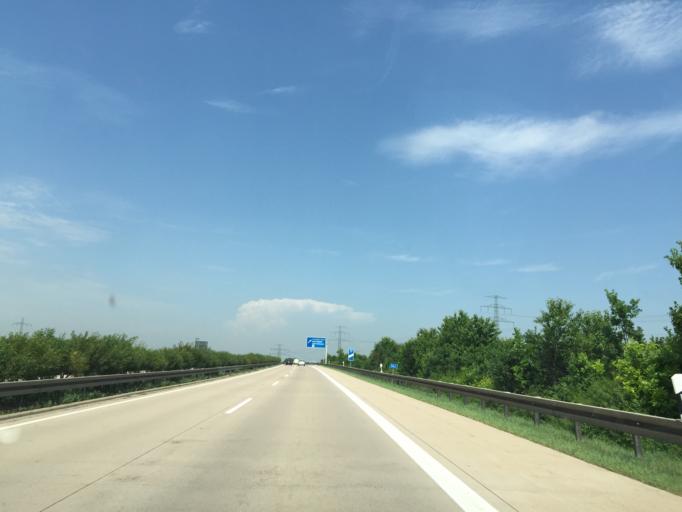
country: DE
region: Thuringia
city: Alkersleben
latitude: 50.8491
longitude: 11.0102
